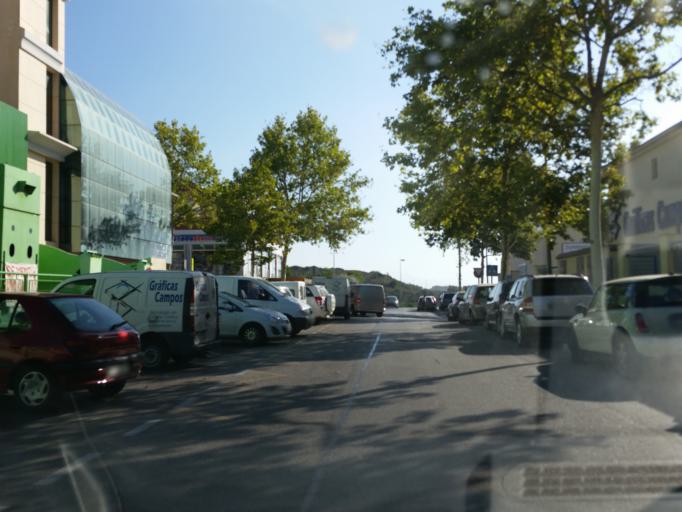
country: ES
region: Andalusia
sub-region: Provincia de Malaga
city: Torremolinos
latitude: 36.6058
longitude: -4.5325
